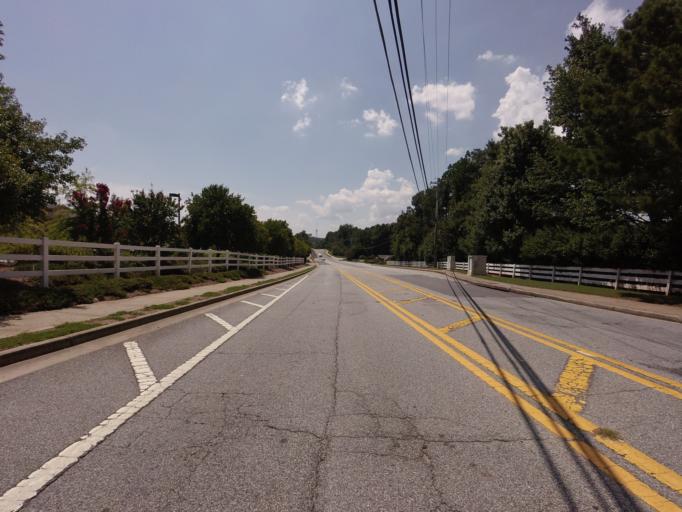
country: US
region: Georgia
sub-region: Fulton County
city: Johns Creek
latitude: 34.0406
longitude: -84.2122
